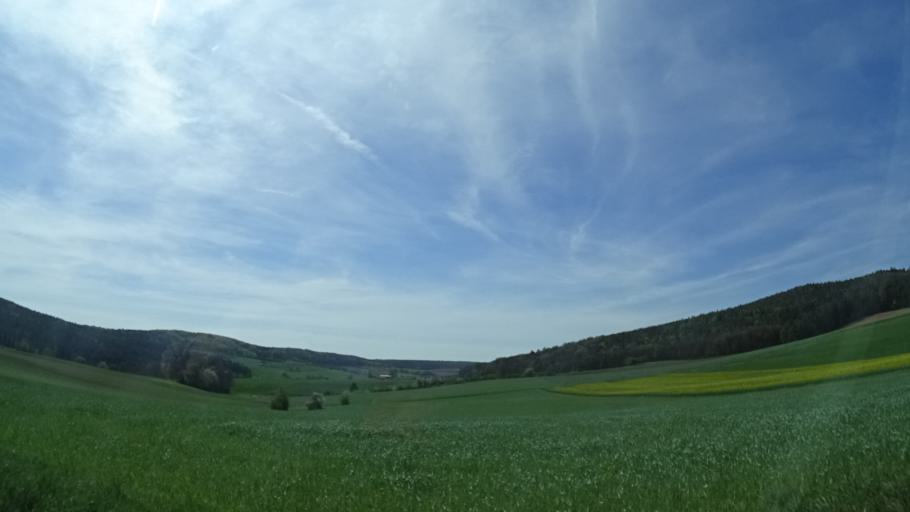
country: DE
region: Bavaria
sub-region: Regierungsbezirk Unterfranken
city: Burgpreppach
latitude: 50.1584
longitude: 10.6351
